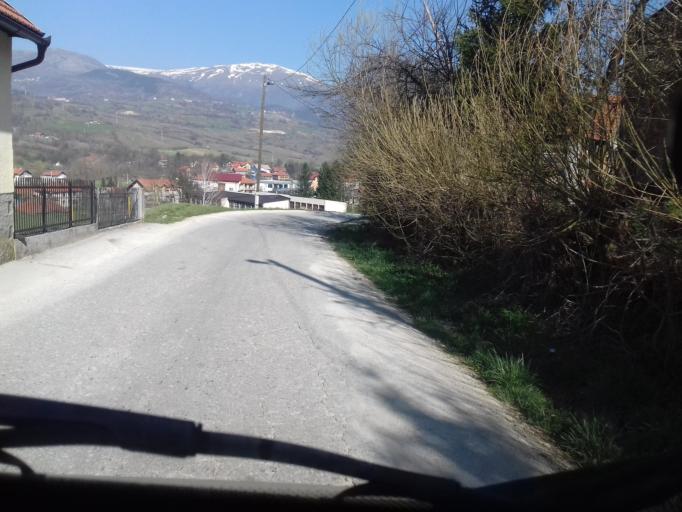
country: BA
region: Federation of Bosnia and Herzegovina
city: Vitez
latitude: 44.2360
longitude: 17.7613
